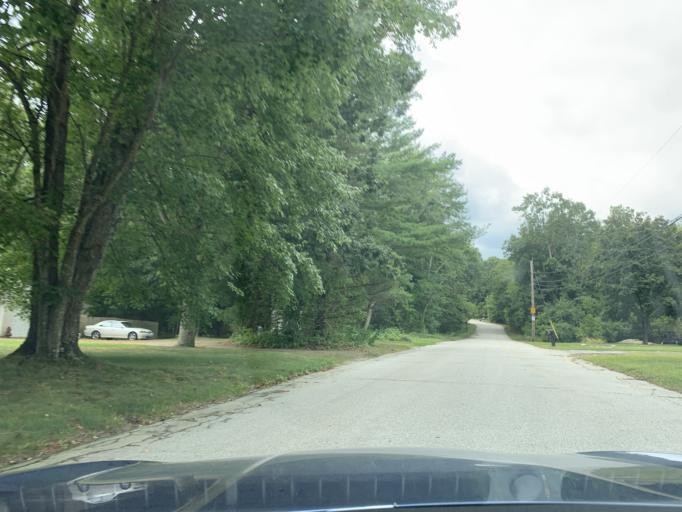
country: US
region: Rhode Island
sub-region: Kent County
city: West Warwick
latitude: 41.7382
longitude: -71.5768
